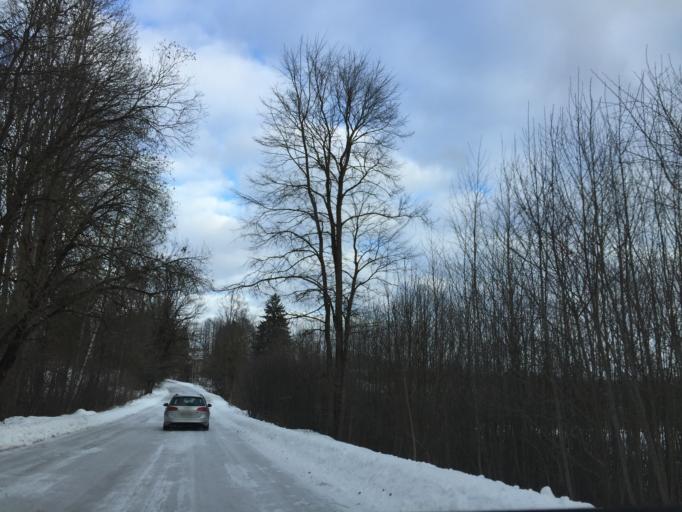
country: LV
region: Lielvarde
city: Lielvarde
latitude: 56.5746
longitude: 24.7358
